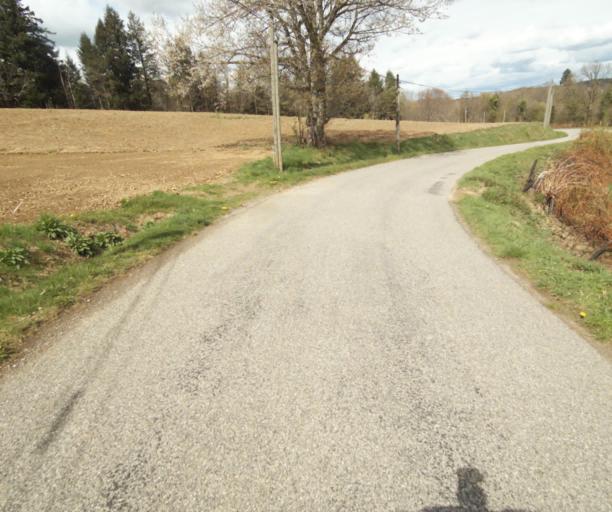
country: FR
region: Limousin
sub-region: Departement de la Correze
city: Laguenne
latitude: 45.2349
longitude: 1.8672
